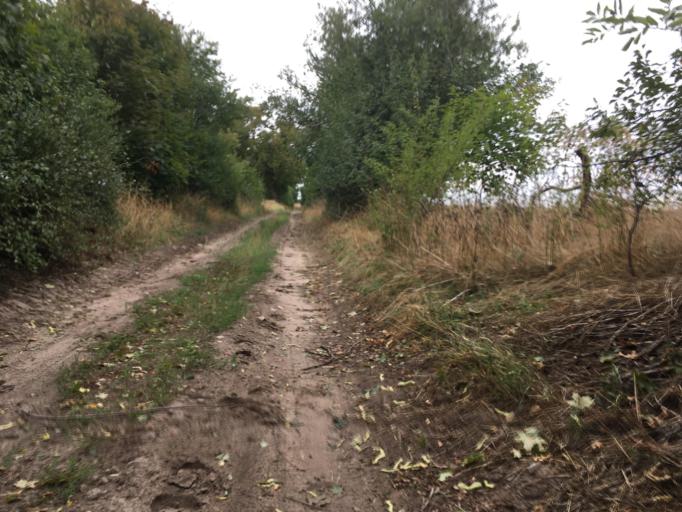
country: DE
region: Brandenburg
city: Passow
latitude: 53.1288
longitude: 14.1065
